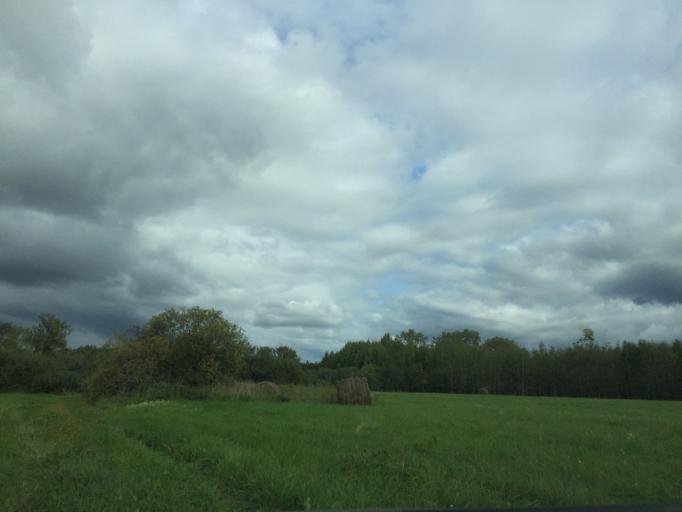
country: LV
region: Pargaujas
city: Stalbe
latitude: 57.4948
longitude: 24.9133
